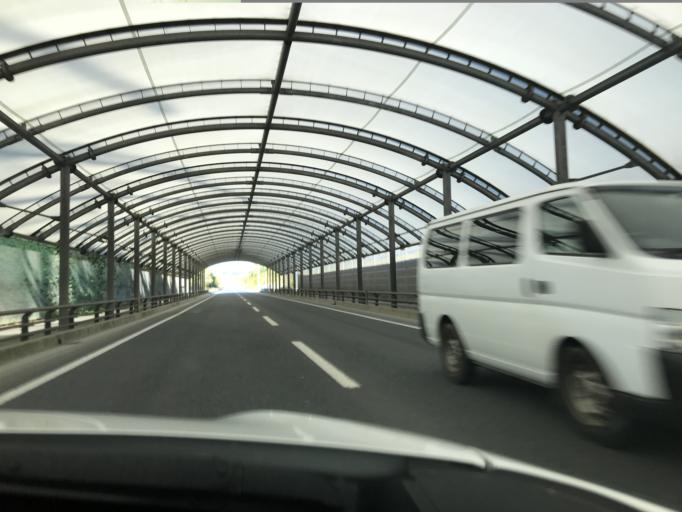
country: JP
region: Miyagi
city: Marumori
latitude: 37.7802
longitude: 140.9402
